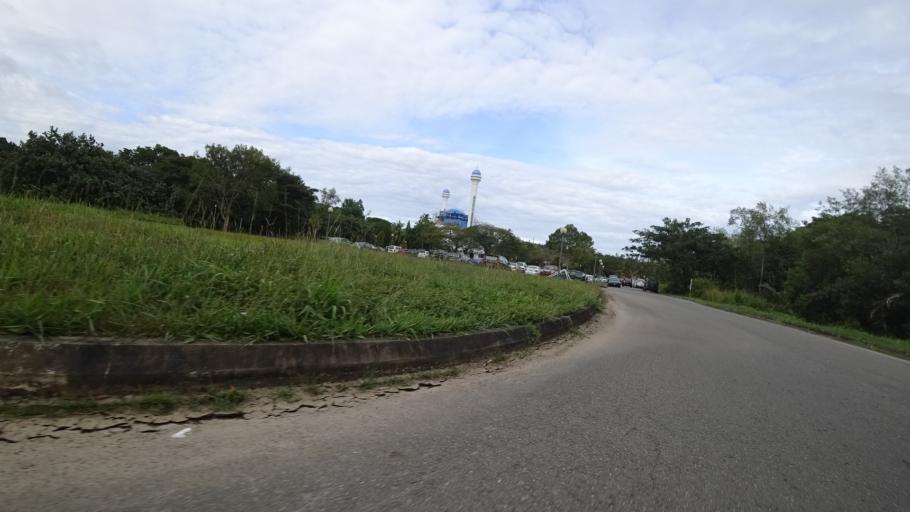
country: BN
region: Brunei and Muara
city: Bandar Seri Begawan
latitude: 4.8517
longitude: 114.9547
